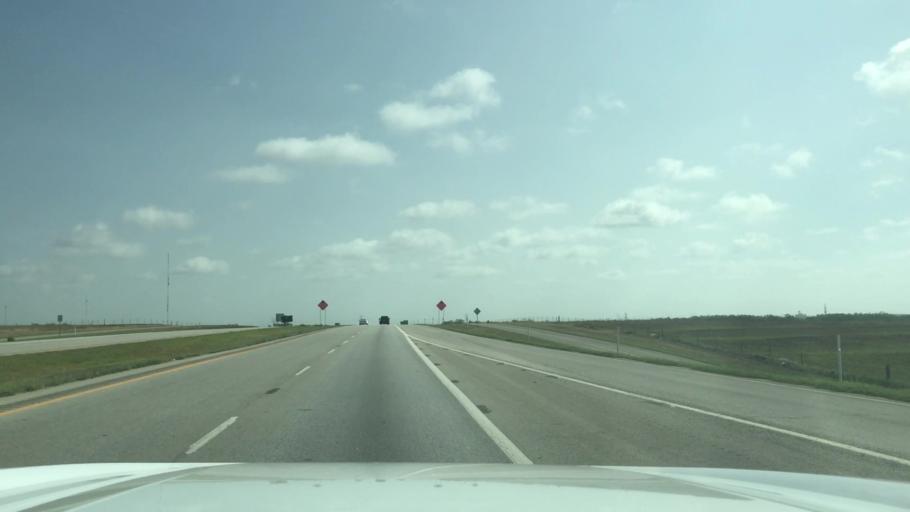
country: US
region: Texas
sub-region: Nolan County
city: Sweetwater
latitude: 32.4673
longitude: -100.3802
